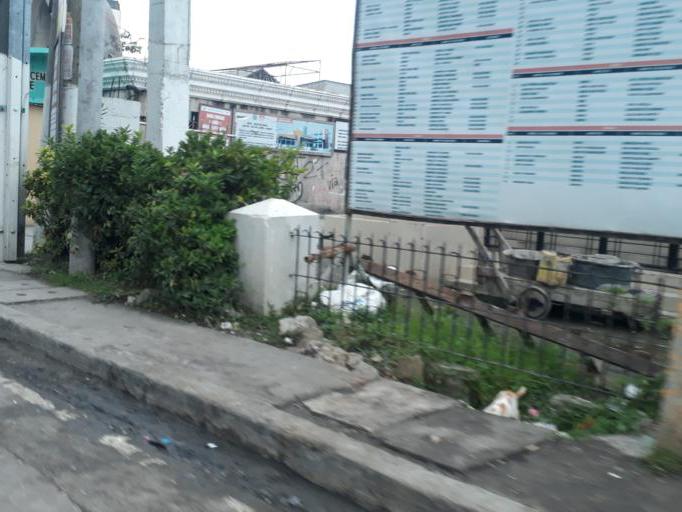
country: PH
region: Calabarzon
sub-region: Province of Rizal
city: Navotas
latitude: 14.6637
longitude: 120.9426
